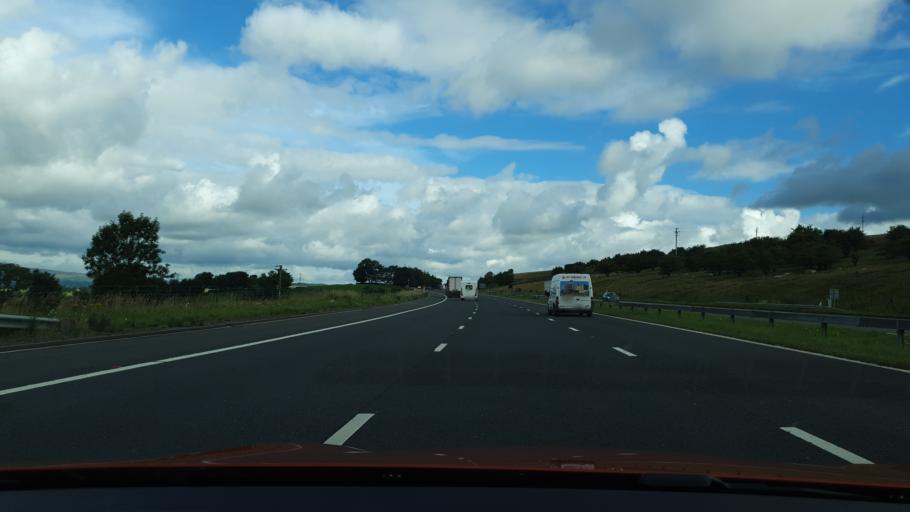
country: GB
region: England
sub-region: Cumbria
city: Appleby-in-Westmorland
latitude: 54.5156
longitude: -2.6535
